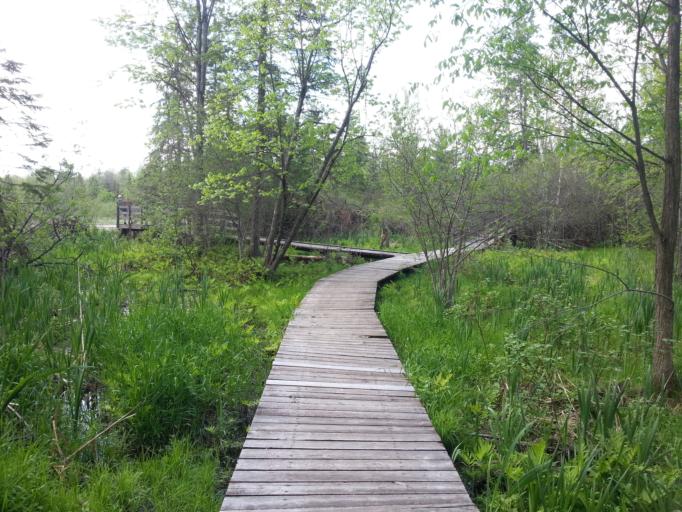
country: CA
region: Ontario
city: Bells Corners
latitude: 45.2936
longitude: -75.8232
